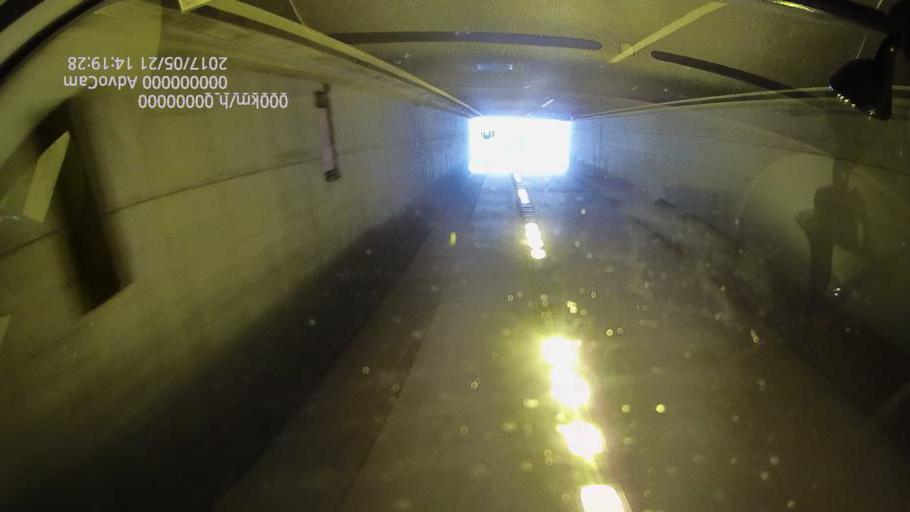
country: GR
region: Central Greece
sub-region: Nomos Fthiotidos
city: Kamena Vourla
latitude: 38.7762
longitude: 22.7992
